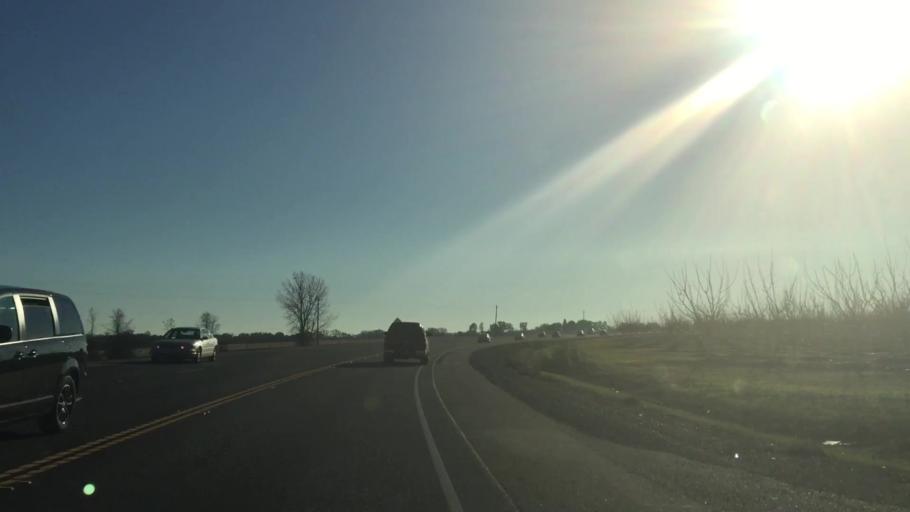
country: US
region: California
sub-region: Butte County
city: Palermo
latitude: 39.3934
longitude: -121.6058
